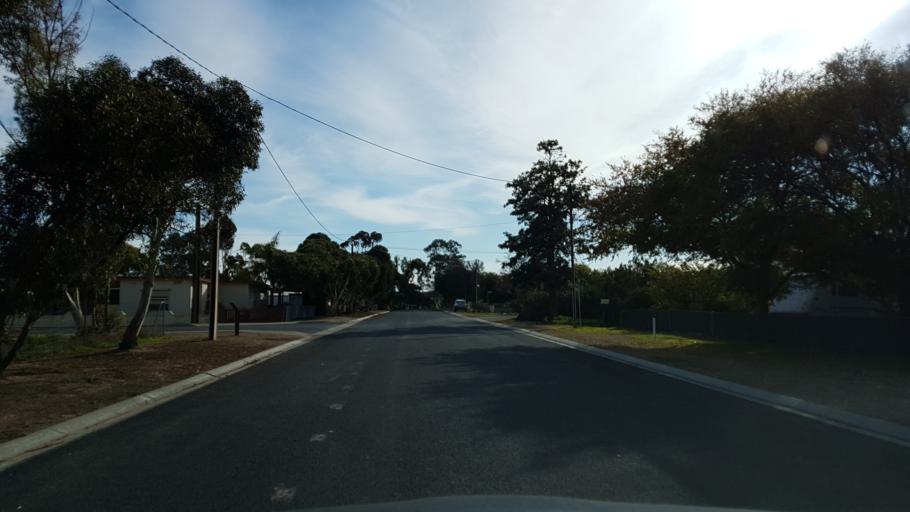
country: AU
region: South Australia
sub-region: Murray Bridge
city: Tailem Bend
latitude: -35.2520
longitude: 139.4626
